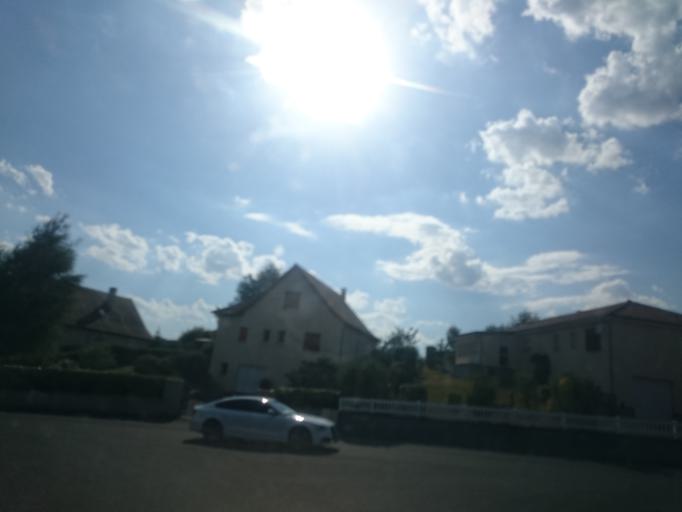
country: FR
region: Auvergne
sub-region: Departement du Cantal
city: Saint-Mamet-la-Salvetat
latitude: 44.8571
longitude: 2.2258
